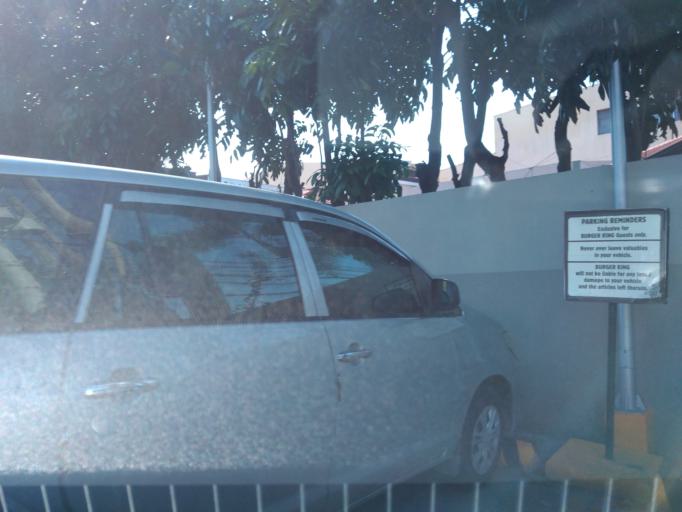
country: PH
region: Calabarzon
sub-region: Province of Laguna
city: Calamba
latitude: 14.1940
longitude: 121.1648
